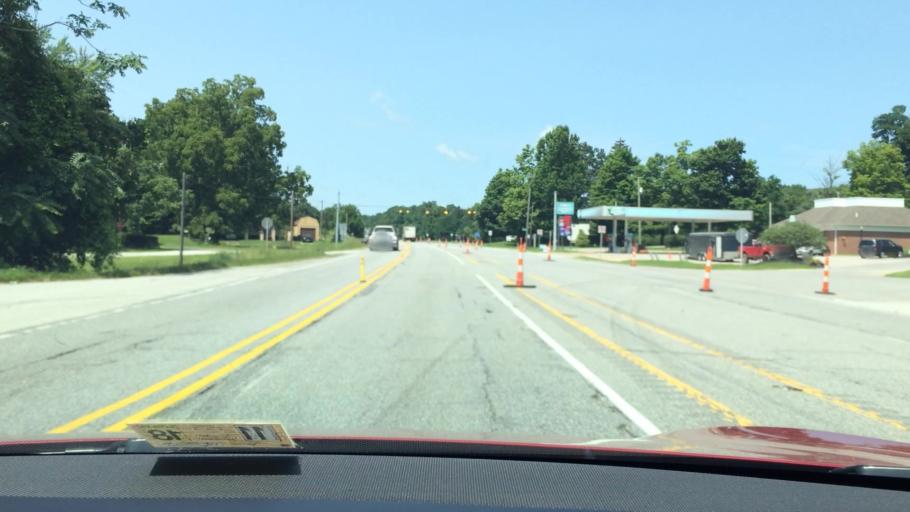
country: US
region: Indiana
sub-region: LaPorte County
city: Hudson Lake
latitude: 41.6716
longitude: -86.6202
